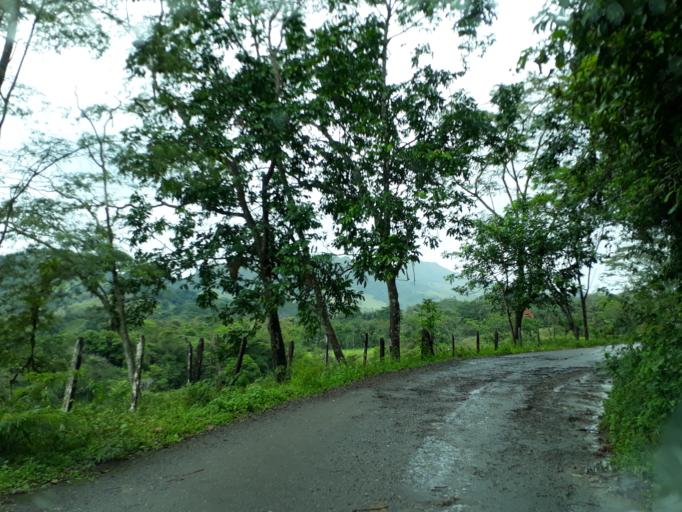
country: CO
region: Boyaca
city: Santa Maria
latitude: 4.6927
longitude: -73.3056
